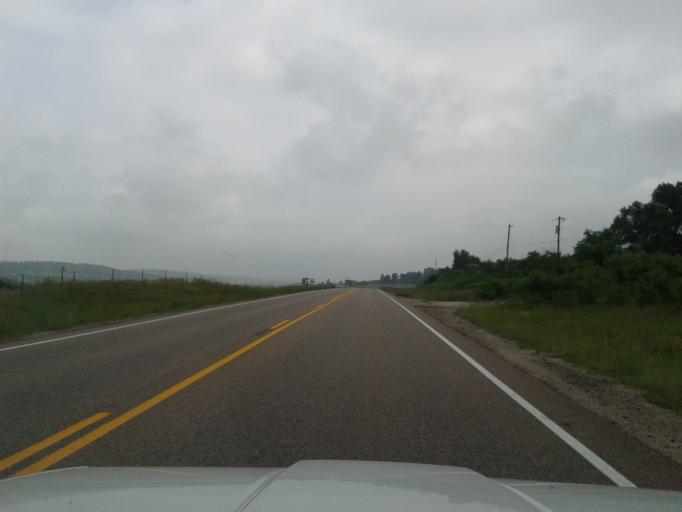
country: US
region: Colorado
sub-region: El Paso County
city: Woodmoor
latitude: 39.1752
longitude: -104.7380
